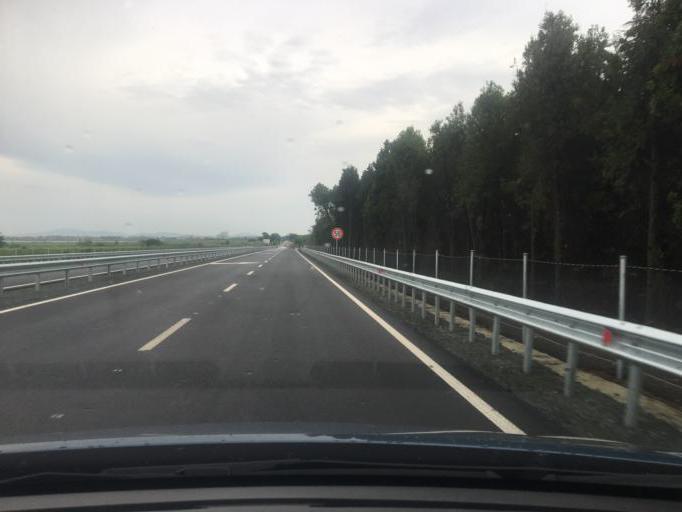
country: BG
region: Burgas
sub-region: Obshtina Pomorie
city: Pomorie
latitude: 42.5977
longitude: 27.6159
